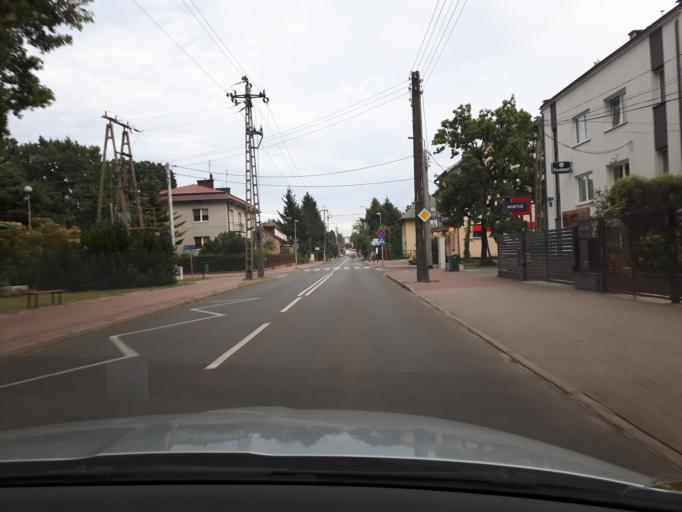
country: PL
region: Masovian Voivodeship
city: Zielonka
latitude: 52.3066
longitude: 21.1570
